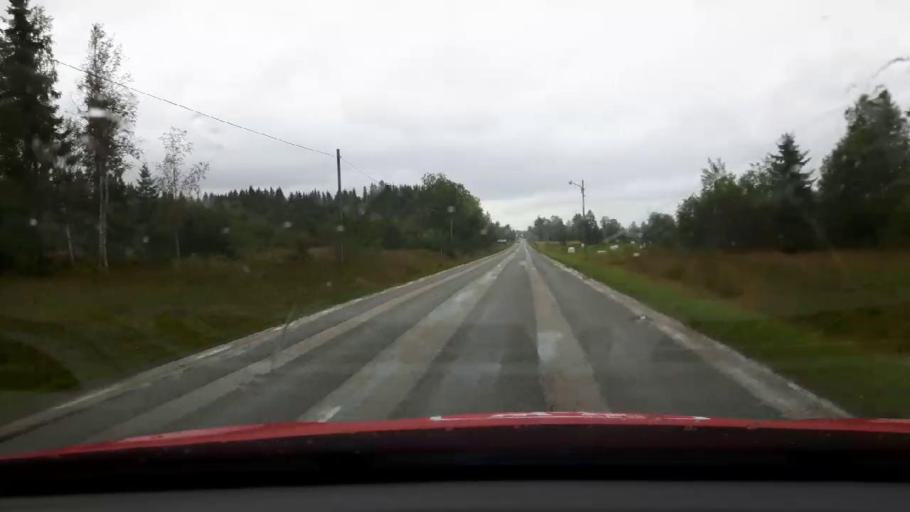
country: SE
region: Jaemtland
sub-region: Bergs Kommun
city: Hoverberg
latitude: 62.8263
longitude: 14.3908
